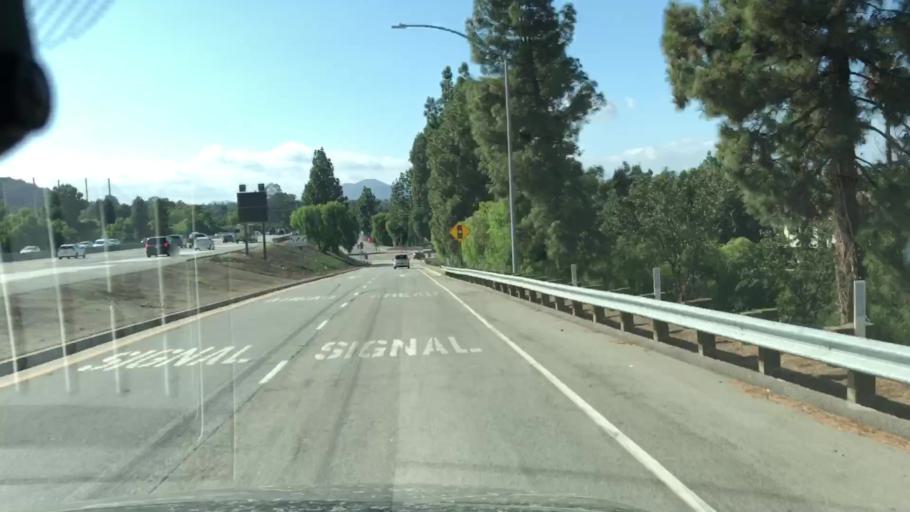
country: US
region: California
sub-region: Ventura County
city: Thousand Oaks
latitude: 34.1775
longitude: -118.8742
